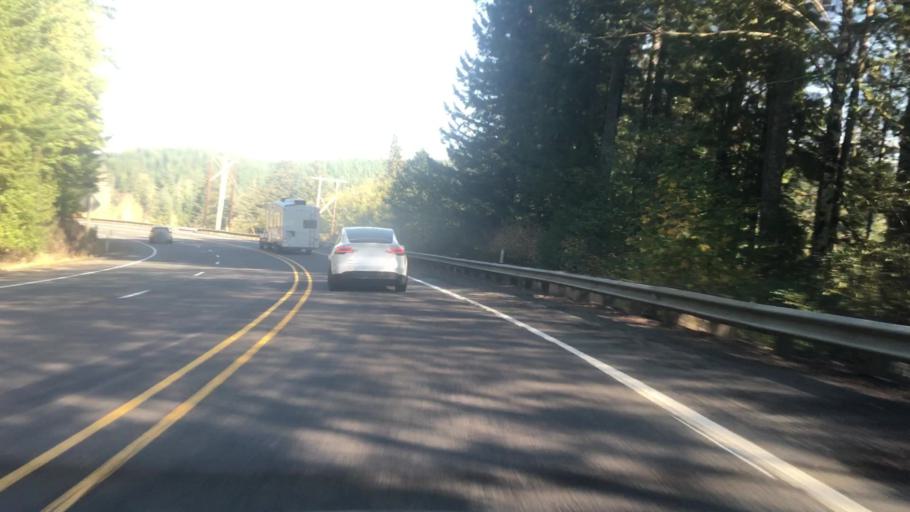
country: US
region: Oregon
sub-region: Polk County
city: Grand Ronde
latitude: 45.0635
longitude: -123.7305
